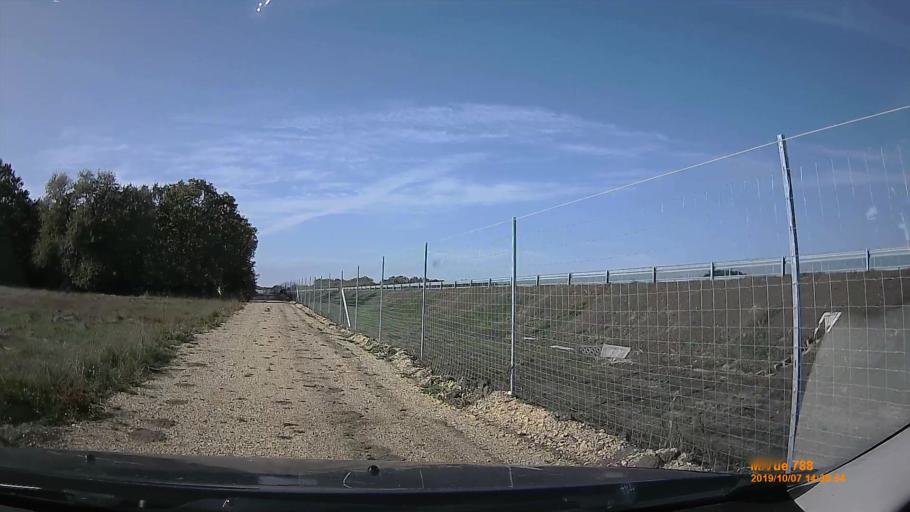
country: HU
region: Jasz-Nagykun-Szolnok
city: Kunszentmarton
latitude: 46.8548
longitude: 20.3126
